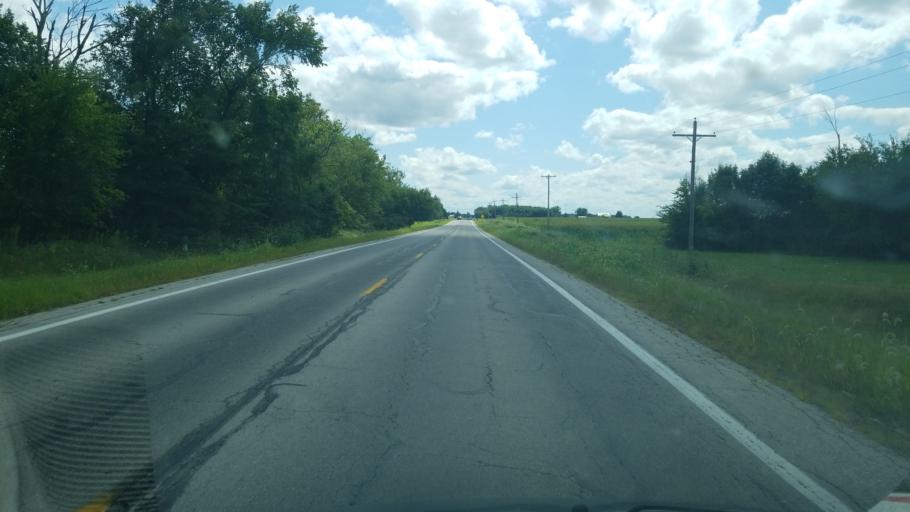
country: US
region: Ohio
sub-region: Henry County
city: Holgate
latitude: 41.3080
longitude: -84.1180
